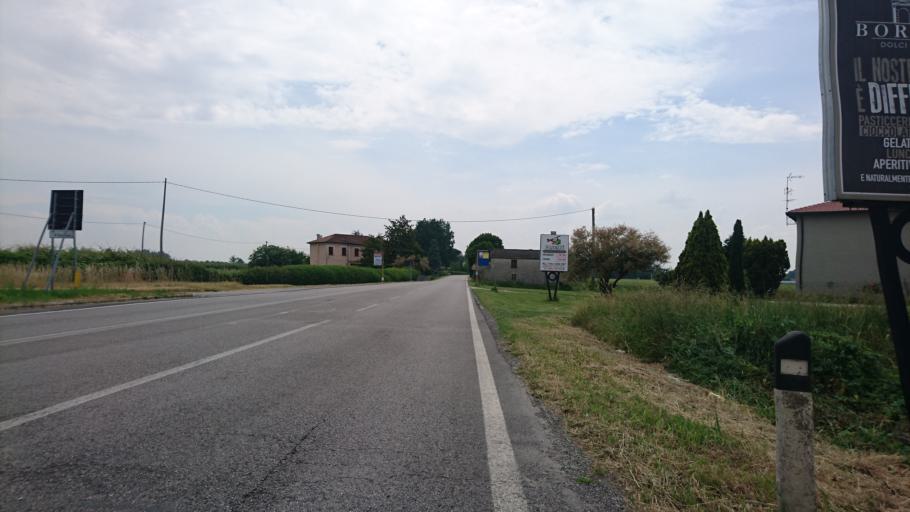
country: IT
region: Veneto
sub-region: Provincia di Rovigo
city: Baruchella
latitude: 45.0777
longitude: 11.4636
